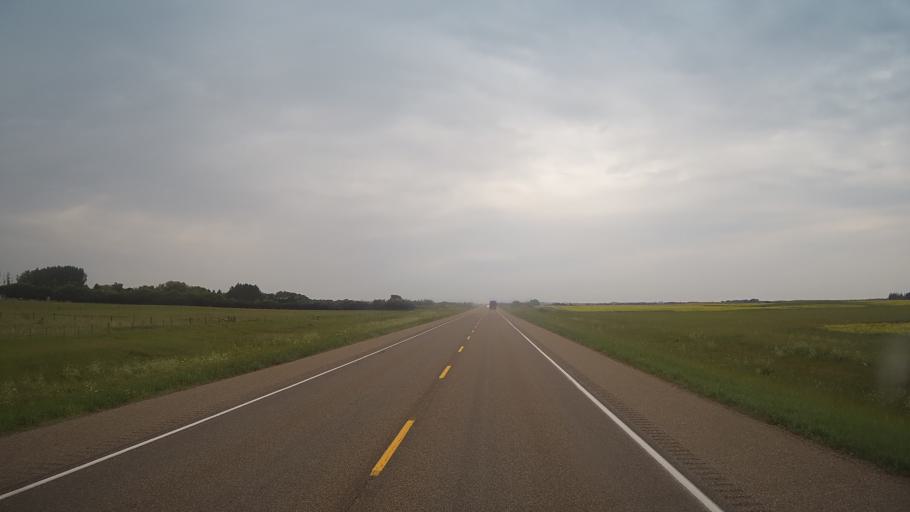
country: CA
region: Saskatchewan
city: Langham
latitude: 52.1293
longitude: -107.0793
